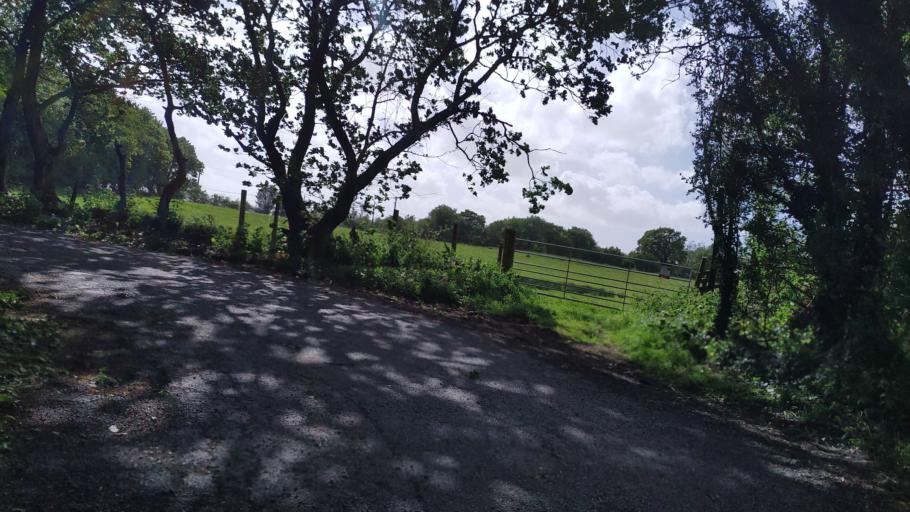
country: GB
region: England
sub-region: Lancashire
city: Chorley
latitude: 53.6452
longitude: -2.5966
